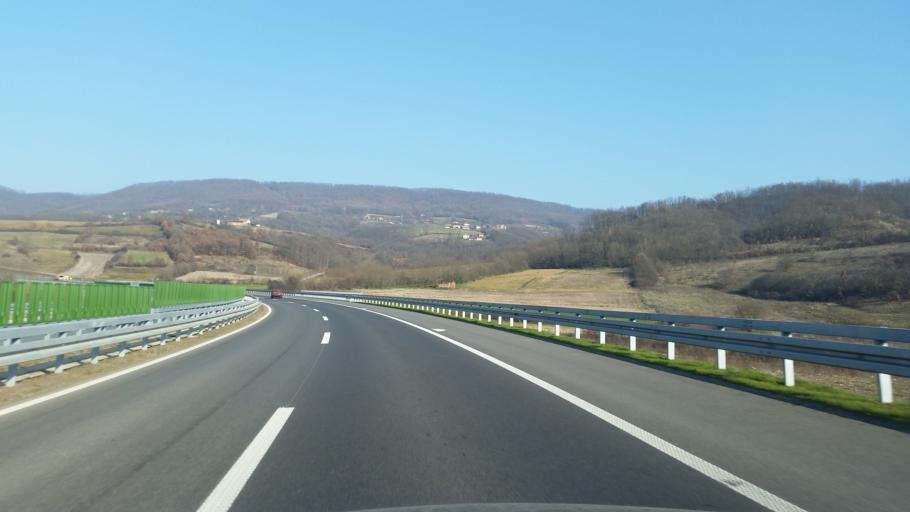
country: RS
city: Prislonica
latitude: 43.9949
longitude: 20.4025
